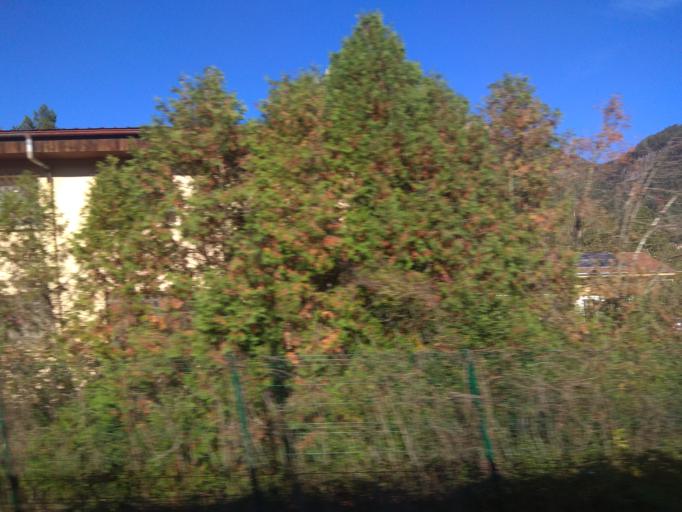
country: FR
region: Rhone-Alpes
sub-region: Departement de la Haute-Savoie
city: Domancy
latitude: 45.9237
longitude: 6.6537
